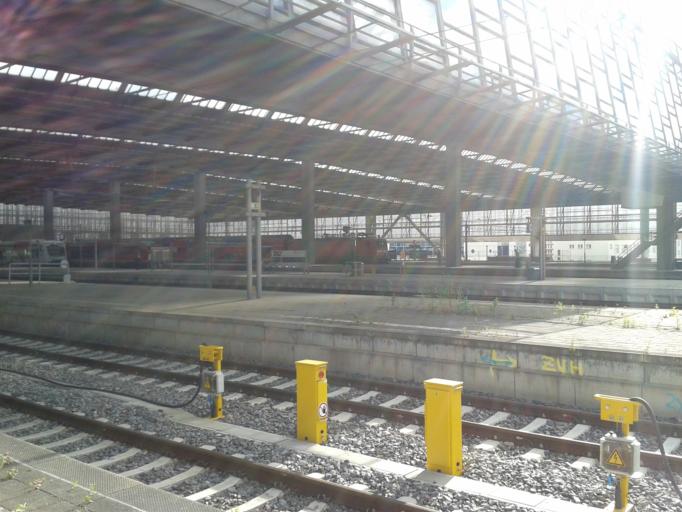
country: DE
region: Saxony
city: Chemnitz
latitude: 50.8407
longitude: 12.9317
